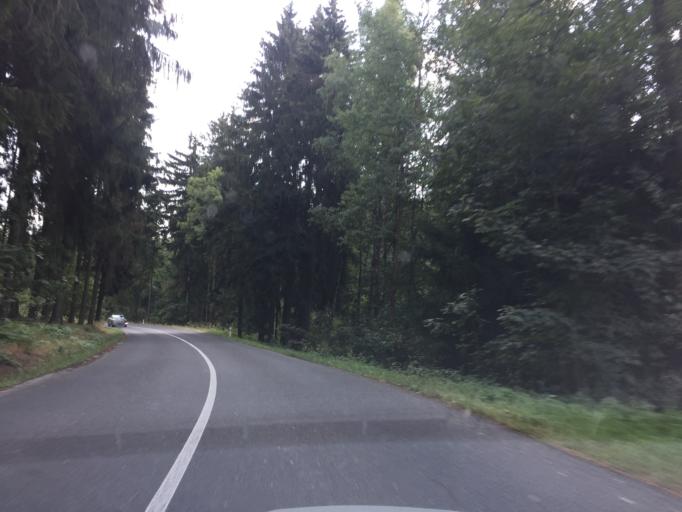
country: CZ
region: Liberecky
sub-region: Okres Jablonec nad Nisou
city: Jablonec nad Nisou
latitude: 50.6935
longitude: 15.1633
